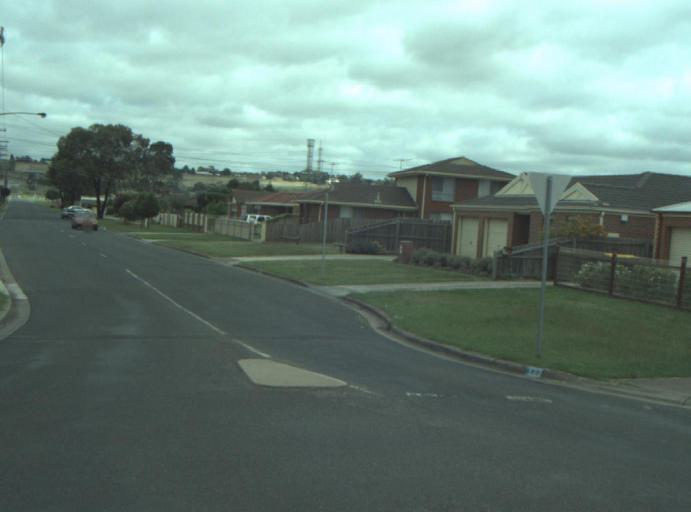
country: AU
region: Victoria
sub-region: Greater Geelong
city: Bell Post Hill
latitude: -38.0768
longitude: 144.3442
